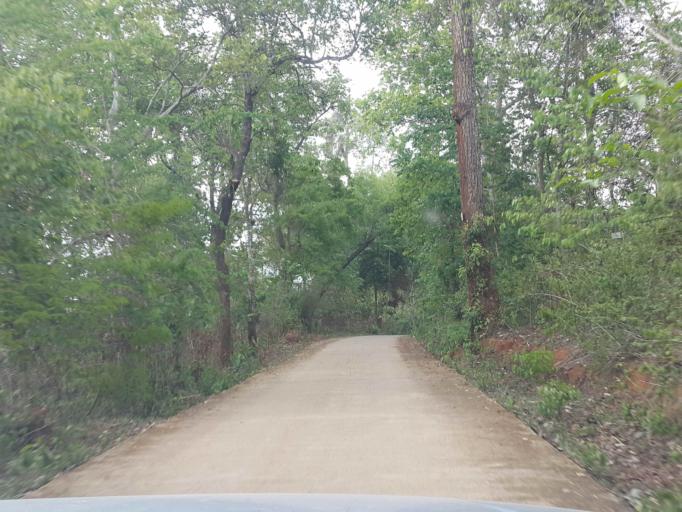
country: TH
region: Chiang Mai
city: Wiang Haeng
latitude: 19.3720
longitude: 98.7194
